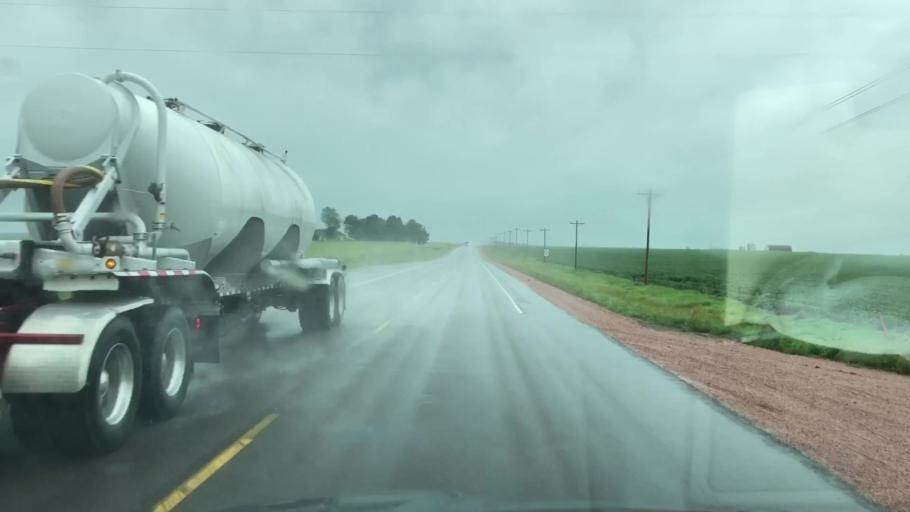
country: US
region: Iowa
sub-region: O'Brien County
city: Sanborn
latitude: 43.1861
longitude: -95.7255
